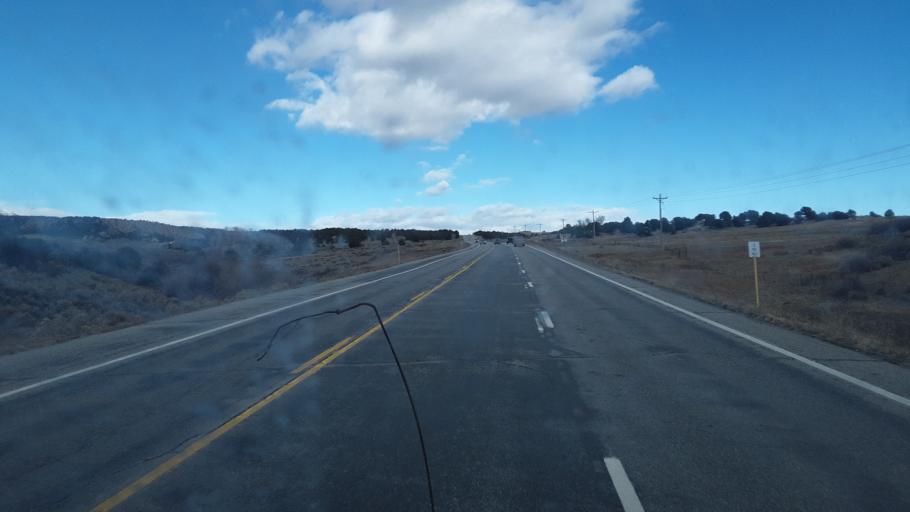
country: US
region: Colorado
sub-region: Chaffee County
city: Salida
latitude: 38.6498
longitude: -106.0847
